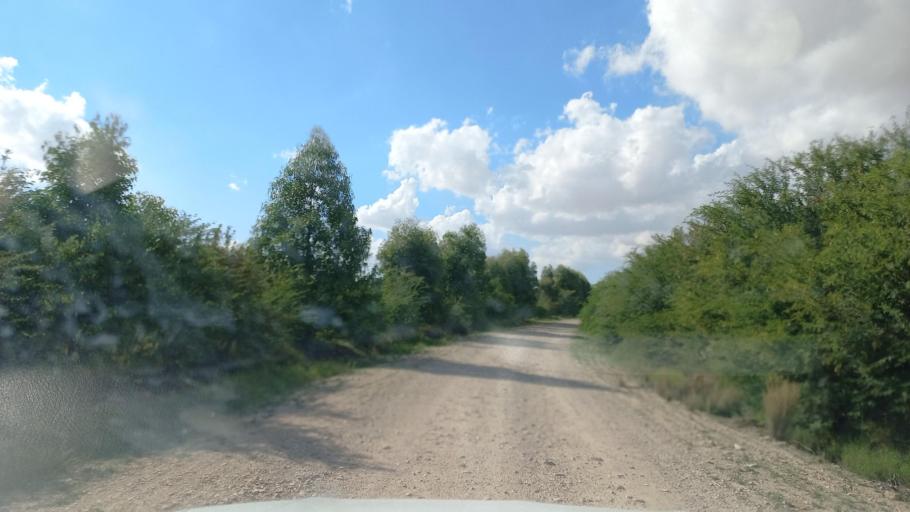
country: TN
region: Al Qasrayn
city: Sbiba
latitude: 35.3359
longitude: 9.0819
